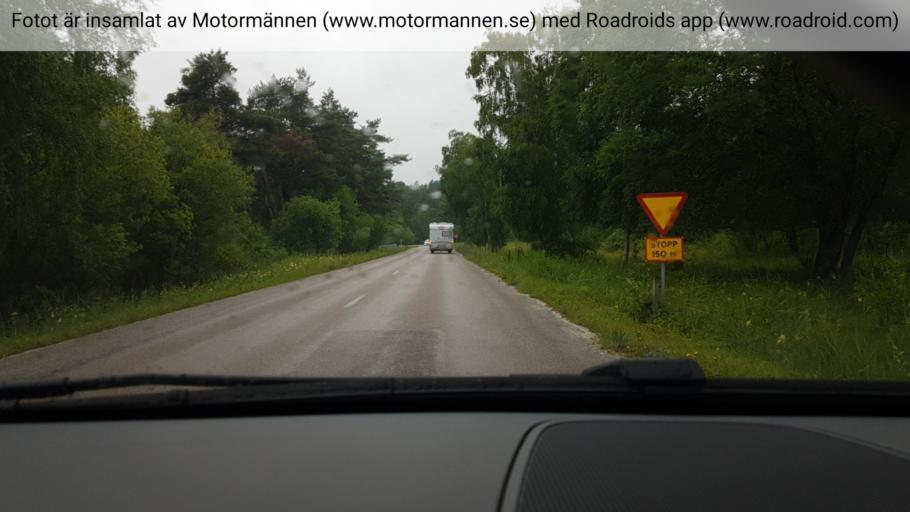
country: SE
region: Gotland
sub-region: Gotland
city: Slite
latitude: 57.8256
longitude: 18.7939
